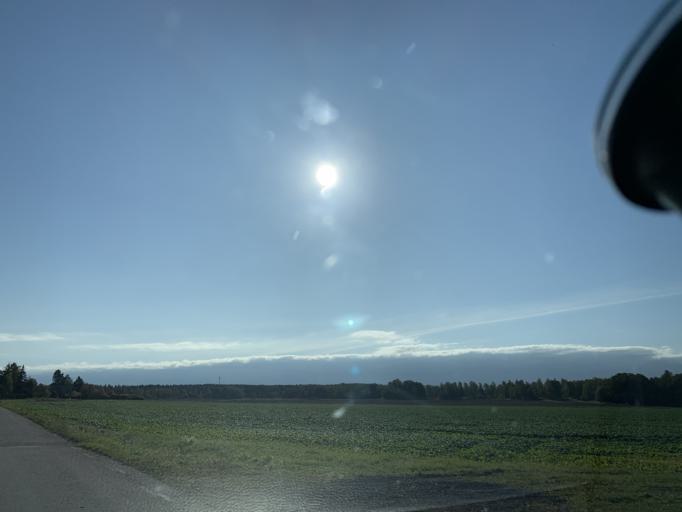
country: SE
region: Vaestmanland
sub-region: Hallstahammars Kommun
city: Kolback
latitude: 59.5506
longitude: 16.3392
